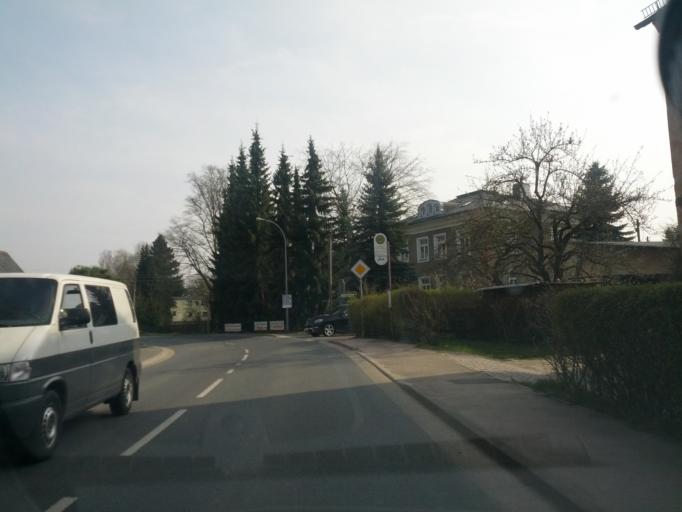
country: DE
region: Saxony
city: Kirchberg
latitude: 50.6094
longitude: 12.5419
